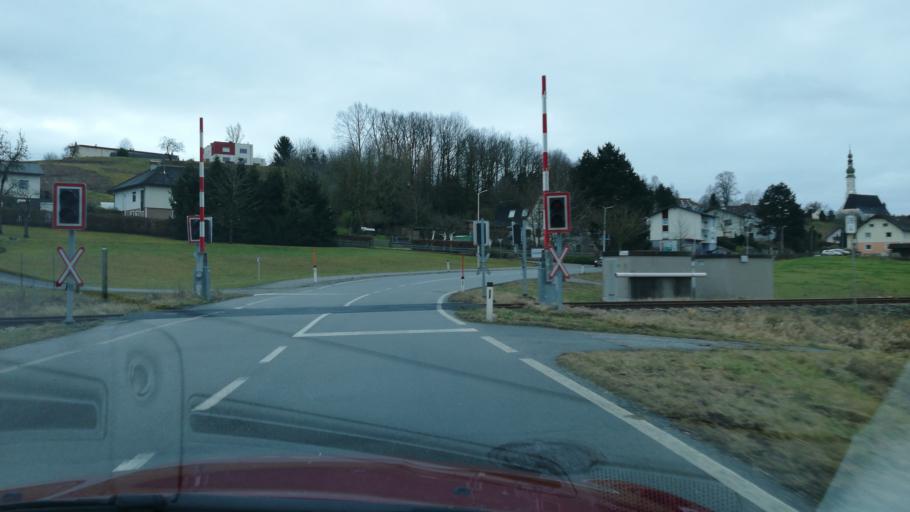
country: AT
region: Upper Austria
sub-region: Politischer Bezirk Braunau am Inn
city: Altheim
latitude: 48.2670
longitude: 13.2984
